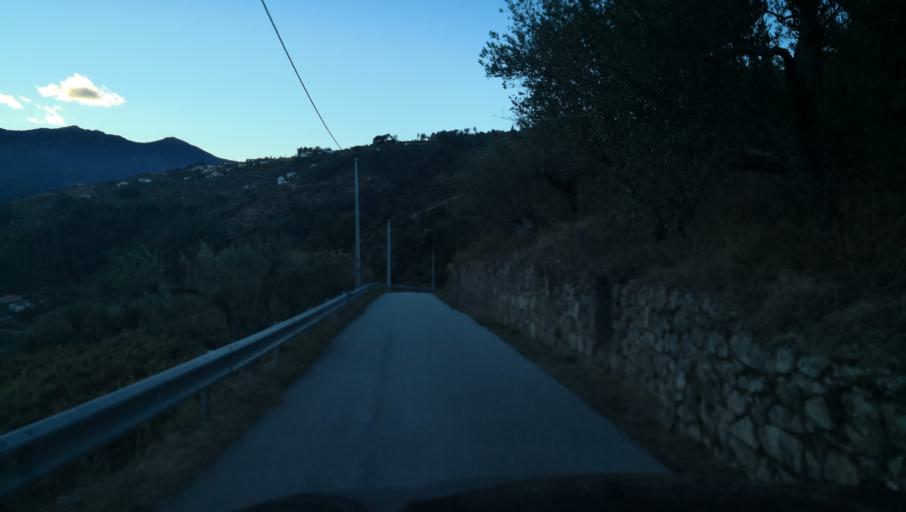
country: PT
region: Vila Real
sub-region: Santa Marta de Penaguiao
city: Santa Marta de Penaguiao
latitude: 41.2567
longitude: -7.7936
